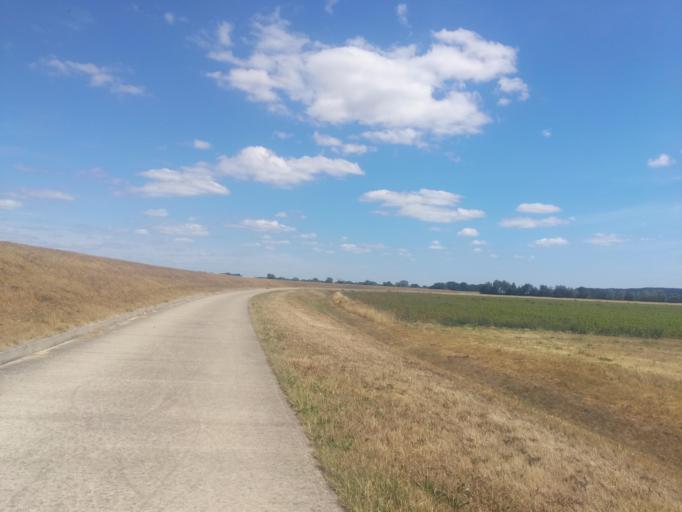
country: DE
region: Lower Saxony
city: Neu Darchau
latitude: 53.2427
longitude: 10.8545
